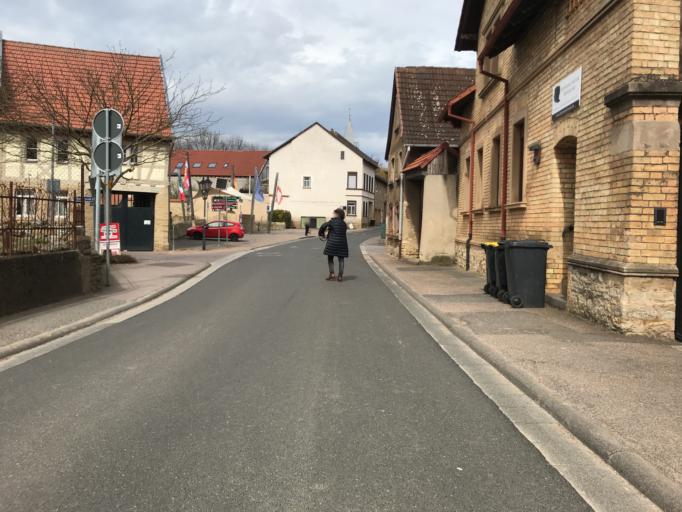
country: DE
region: Rheinland-Pfalz
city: Ober-Hilbersheim
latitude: 49.9003
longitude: 8.0300
